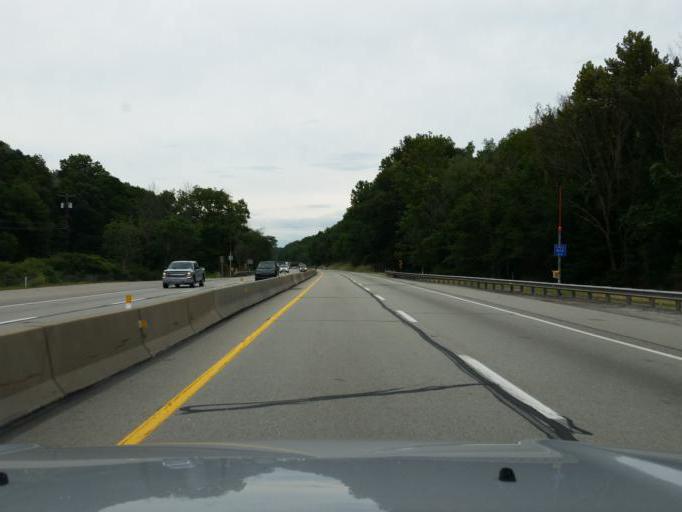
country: US
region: Pennsylvania
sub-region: Westmoreland County
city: Level Green
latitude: 40.3918
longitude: -79.6879
